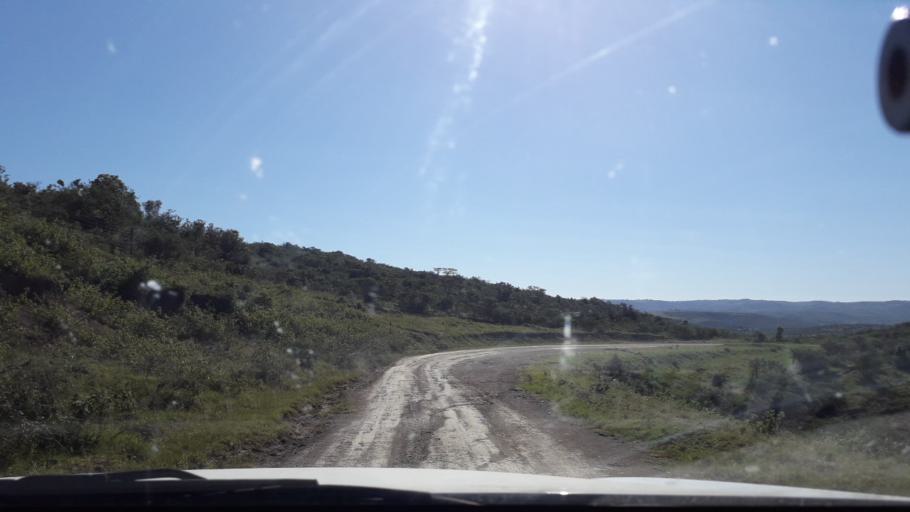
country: ZA
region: Eastern Cape
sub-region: Amathole District Municipality
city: Komga
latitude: -32.7831
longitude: 27.9568
